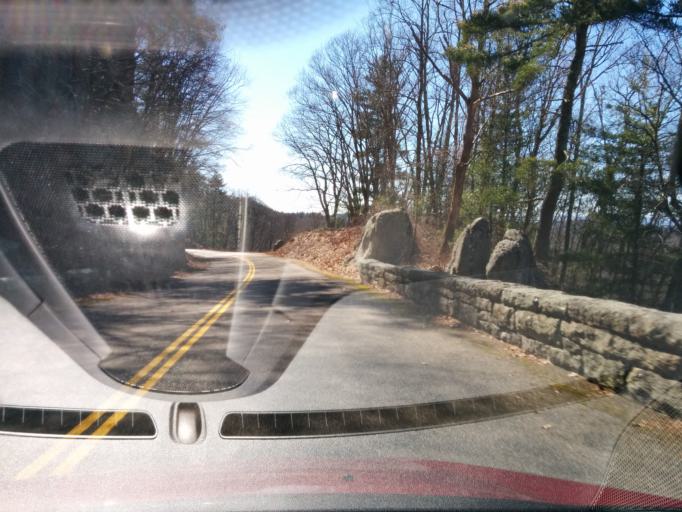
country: US
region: Virginia
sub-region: City of Buena Vista
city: Buena Vista
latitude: 37.8007
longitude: -79.1964
